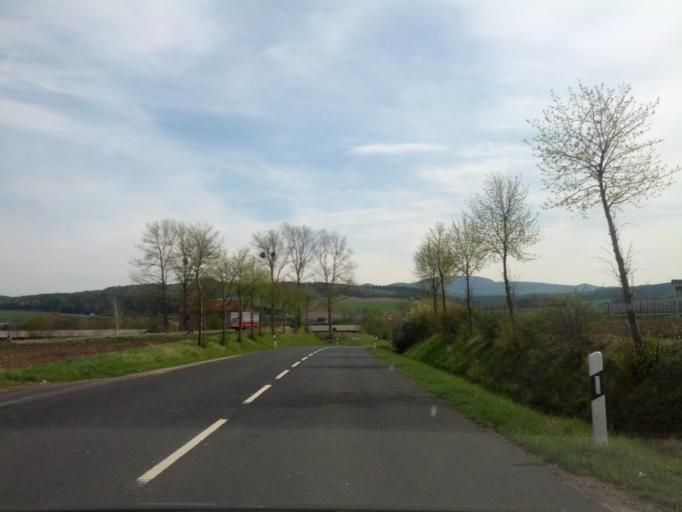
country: DE
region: Thuringia
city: Mechterstadt
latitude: 50.9490
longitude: 10.4881
